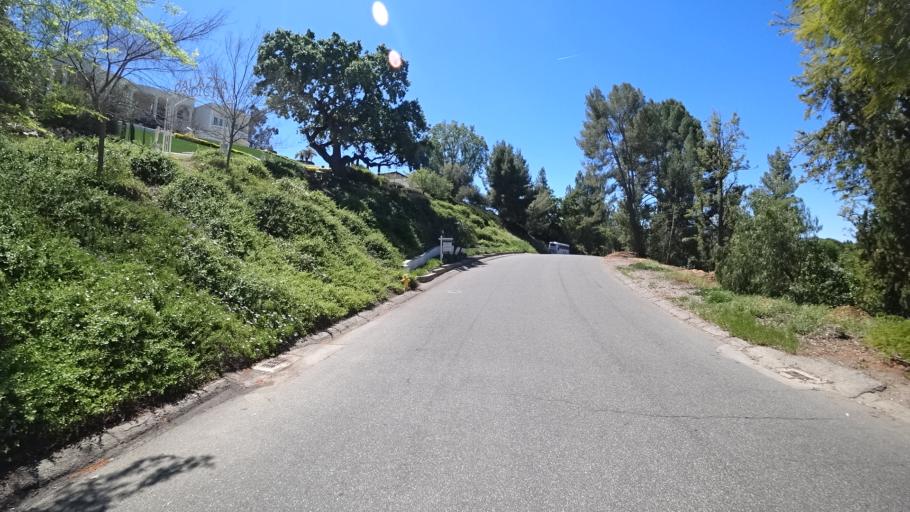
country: US
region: California
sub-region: Ventura County
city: Thousand Oaks
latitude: 34.1900
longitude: -118.8538
